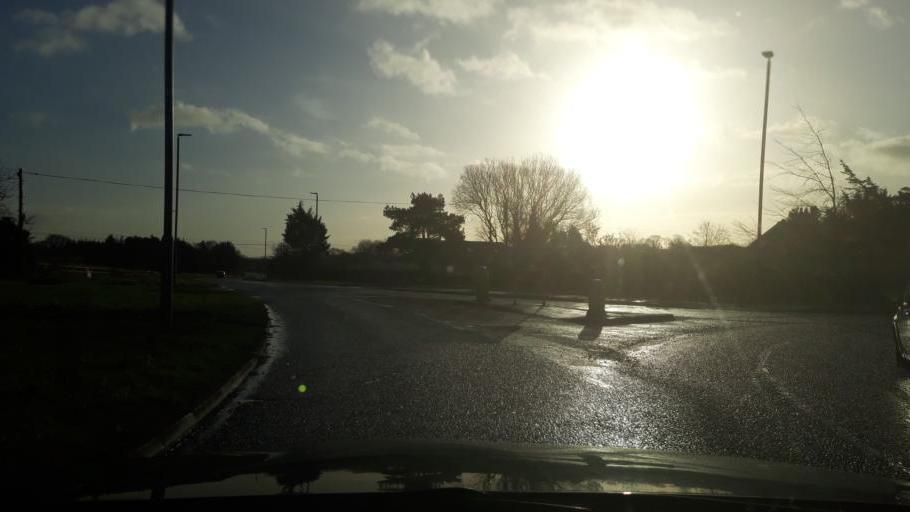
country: GB
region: Northern Ireland
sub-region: Coleraine District
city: Coleraine
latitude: 55.1078
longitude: -6.6937
